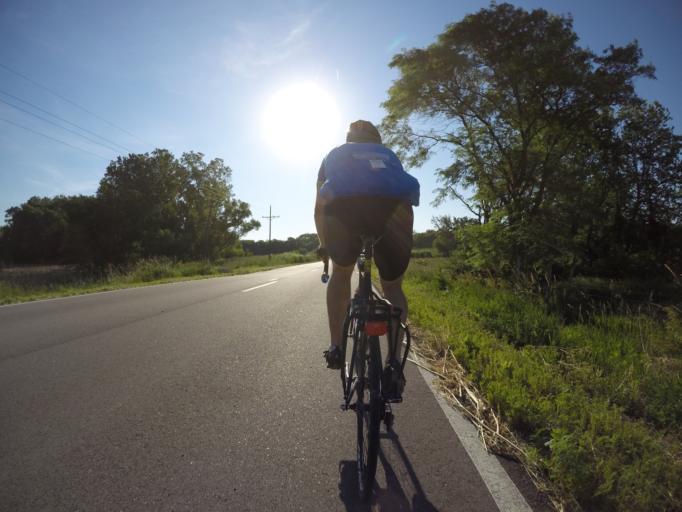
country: US
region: Nebraska
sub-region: Gage County
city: Wymore
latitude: 40.0883
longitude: -96.4888
